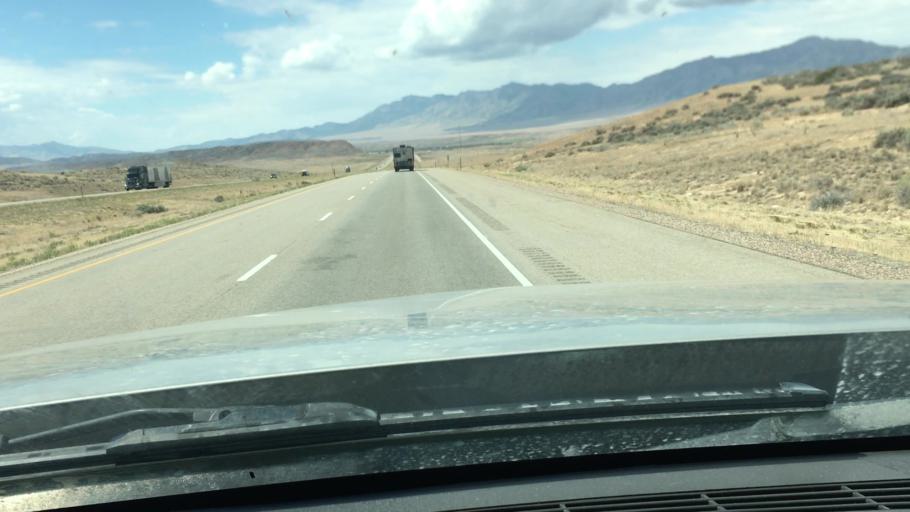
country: US
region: Utah
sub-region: Juab County
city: Nephi
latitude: 39.4638
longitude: -111.9998
